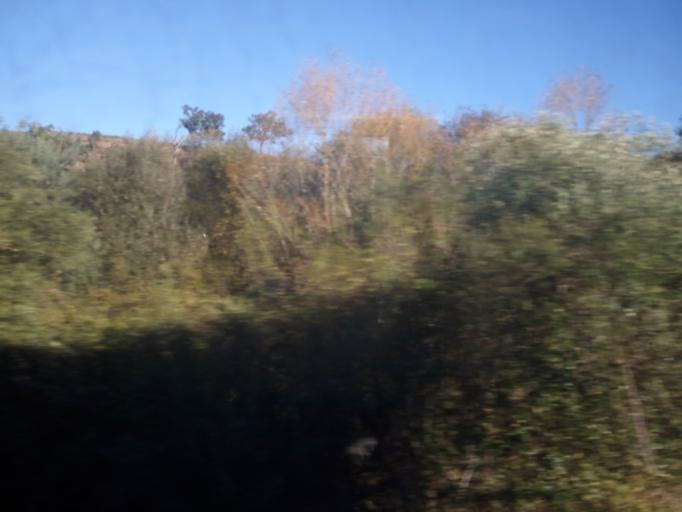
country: PT
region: Beja
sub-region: Odemira
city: Odemira
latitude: 37.5799
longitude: -8.4924
